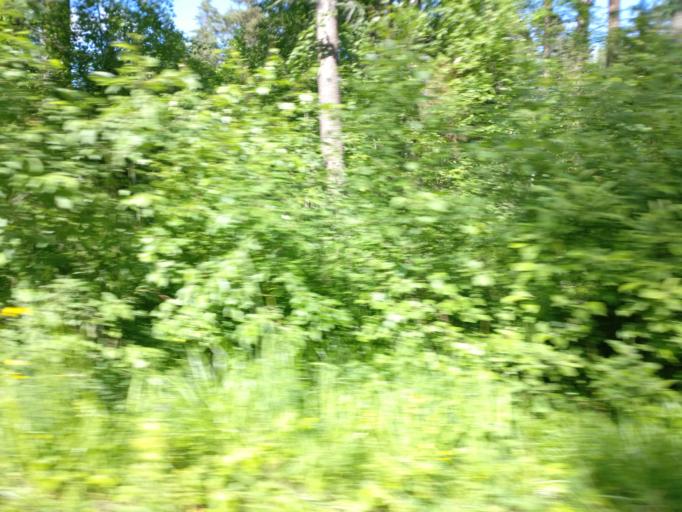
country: FI
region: Southern Savonia
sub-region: Savonlinna
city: Punkaharju
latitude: 61.8010
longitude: 29.3173
